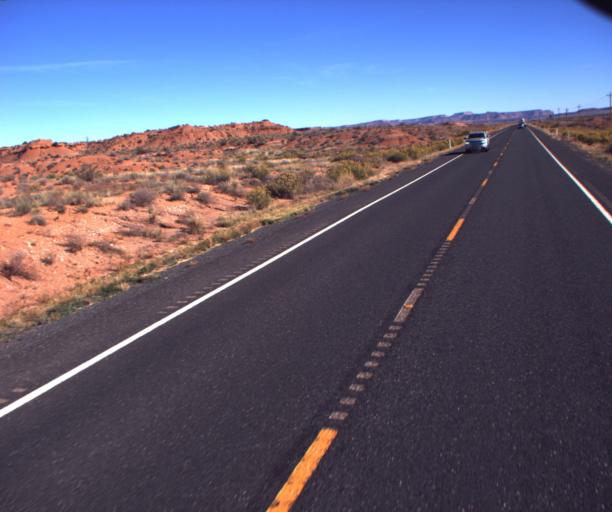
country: US
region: Arizona
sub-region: Coconino County
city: Fredonia
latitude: 36.9140
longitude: -112.5823
